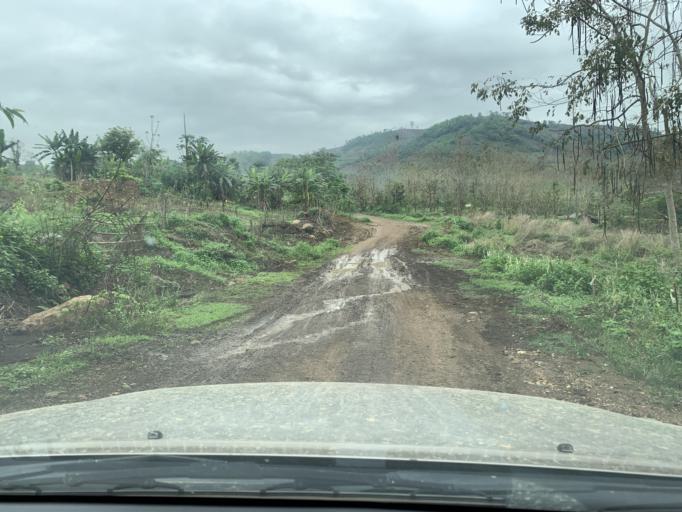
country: TH
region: Uttaradit
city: Ban Khok
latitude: 18.3952
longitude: 101.4296
